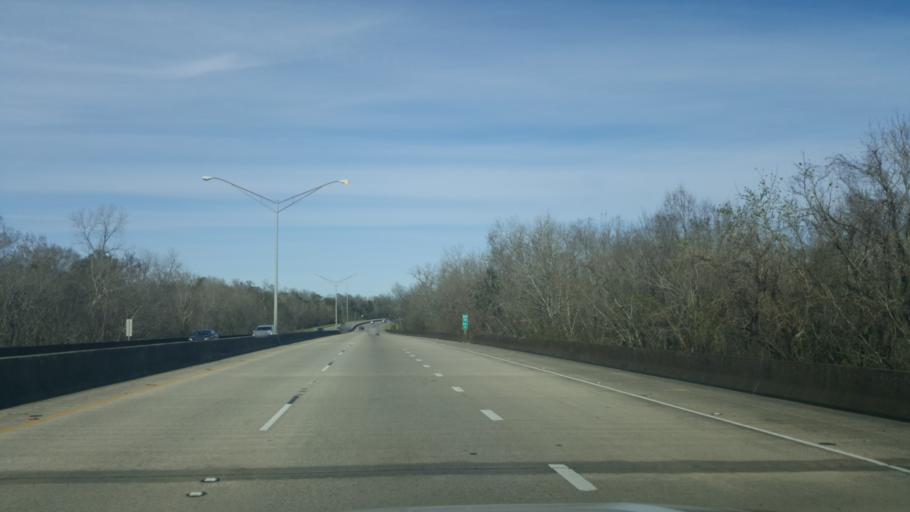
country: US
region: Louisiana
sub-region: Saint Charles Parish
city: Destrehan
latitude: 29.9554
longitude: -90.3660
